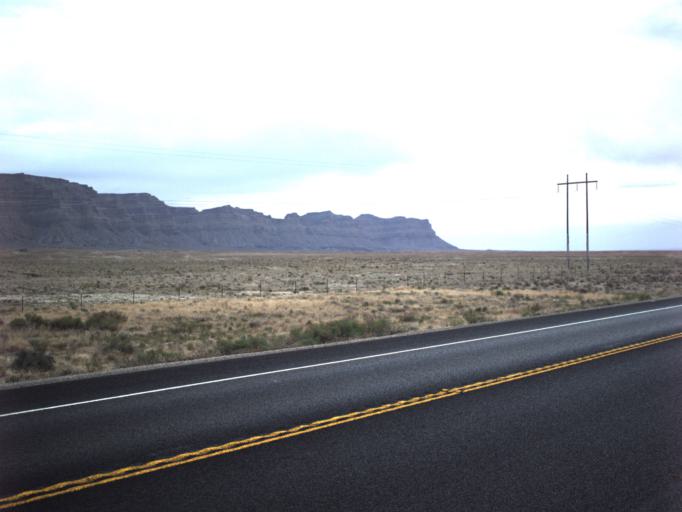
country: US
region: Utah
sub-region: Carbon County
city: East Carbon City
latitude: 39.1824
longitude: -110.3384
